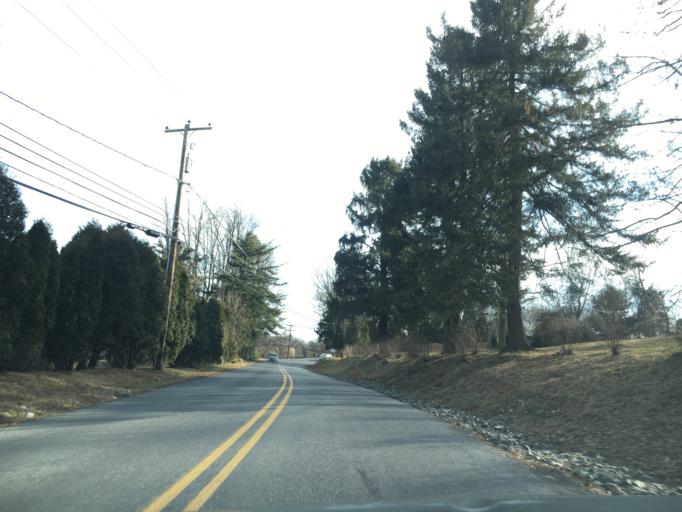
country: US
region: Pennsylvania
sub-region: Berks County
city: South Temple
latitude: 40.3863
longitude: -75.8763
